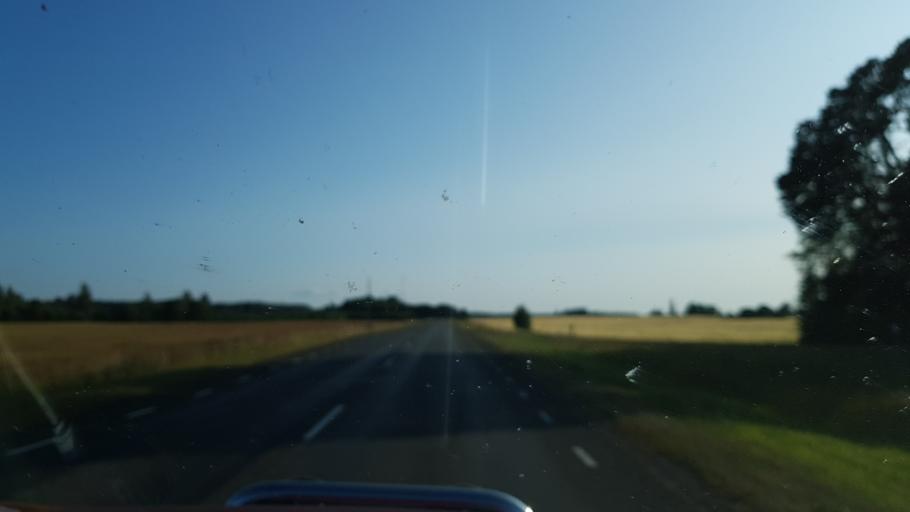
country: EE
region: Harju
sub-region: Raasiku vald
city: Raasiku
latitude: 59.1219
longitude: 25.1916
